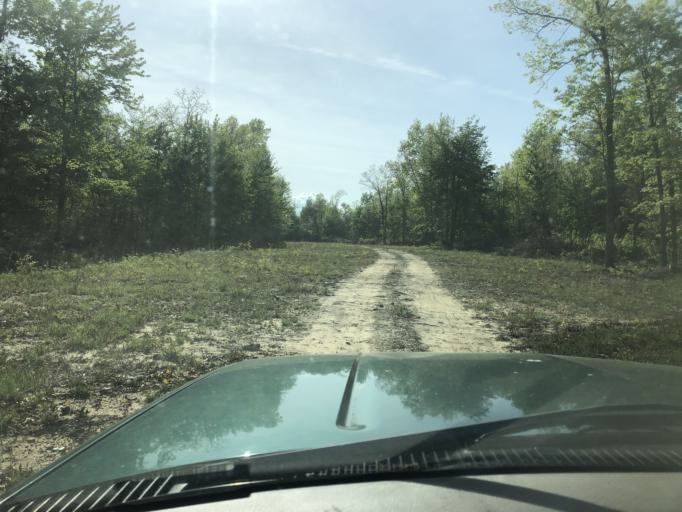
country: US
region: Tennessee
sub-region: Fentress County
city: Jamestown
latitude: 36.3195
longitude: -84.8497
